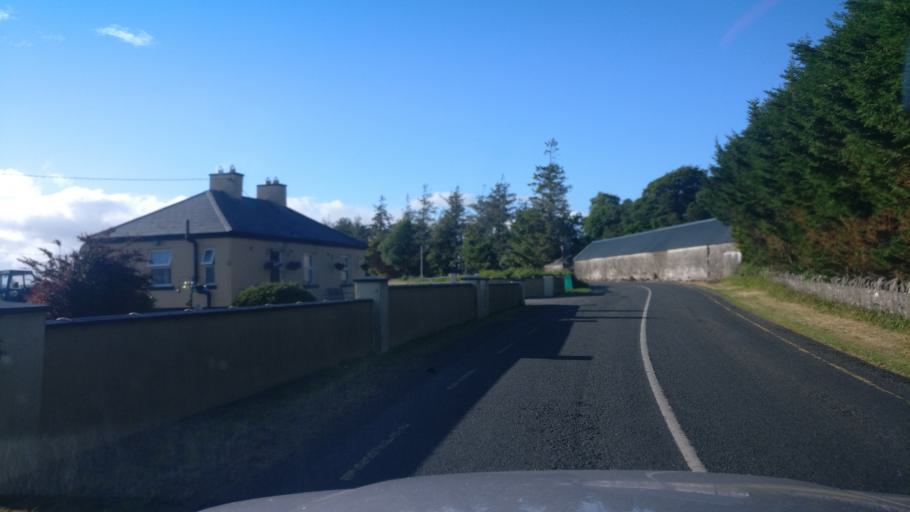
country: IE
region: Connaught
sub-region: County Galway
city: Ballinasloe
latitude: 53.2524
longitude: -8.1777
